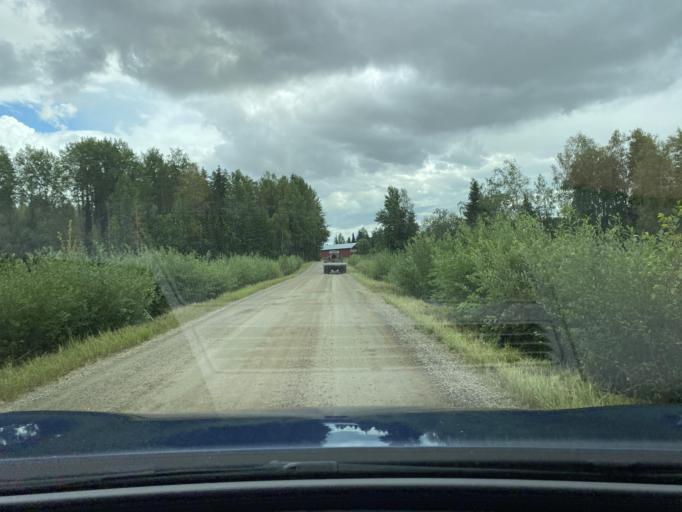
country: FI
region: Pirkanmaa
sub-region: Lounais-Pirkanmaa
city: Punkalaidun
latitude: 61.1730
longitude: 23.1802
